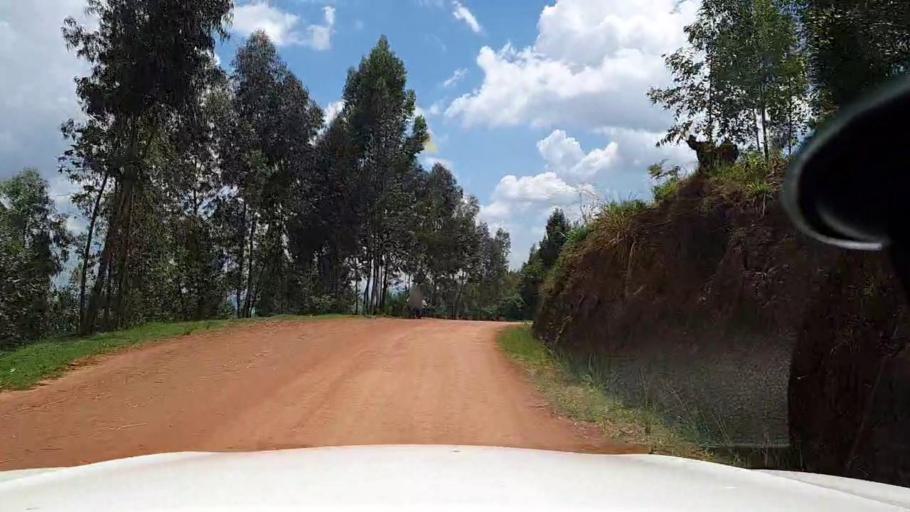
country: RW
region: Kigali
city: Kigali
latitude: -1.7897
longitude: 29.8439
